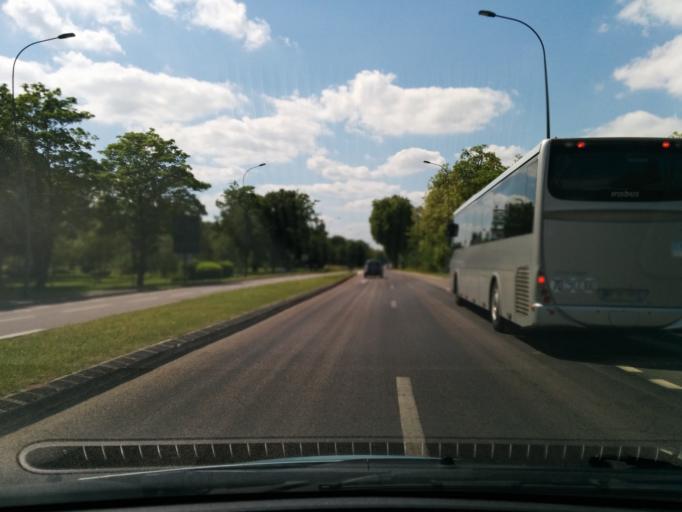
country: FR
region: Ile-de-France
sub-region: Departement des Yvelines
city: Buchelay
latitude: 48.9969
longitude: 1.6759
